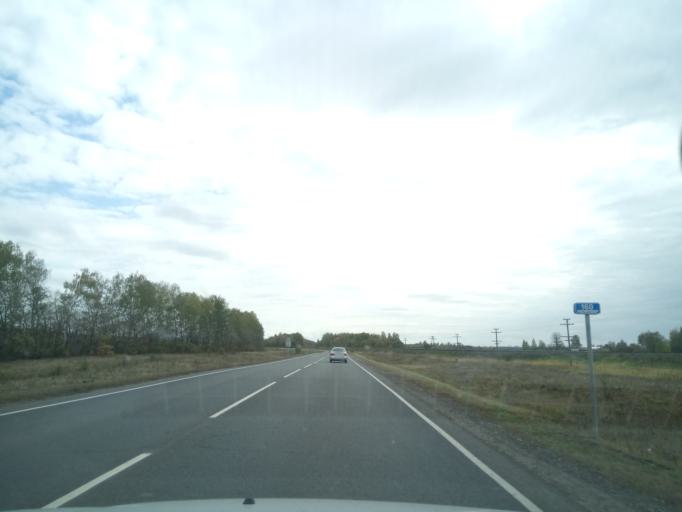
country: RU
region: Nizjnij Novgorod
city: Lukoyanov
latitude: 55.0673
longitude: 44.3463
